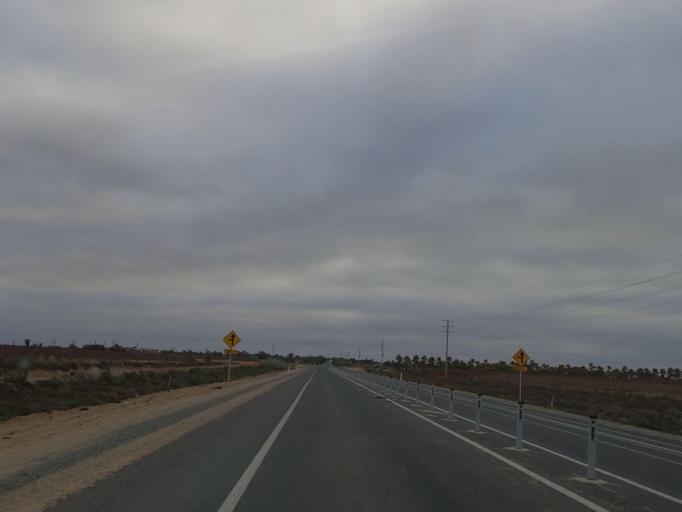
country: AU
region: Victoria
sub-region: Swan Hill
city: Swan Hill
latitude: -35.4725
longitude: 143.6708
